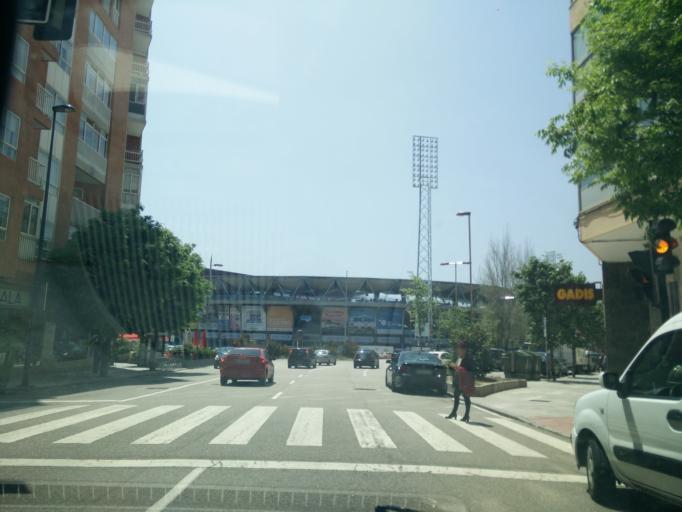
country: ES
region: Galicia
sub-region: Provincia de Pontevedra
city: Vigo
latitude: 42.2136
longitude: -8.7378
